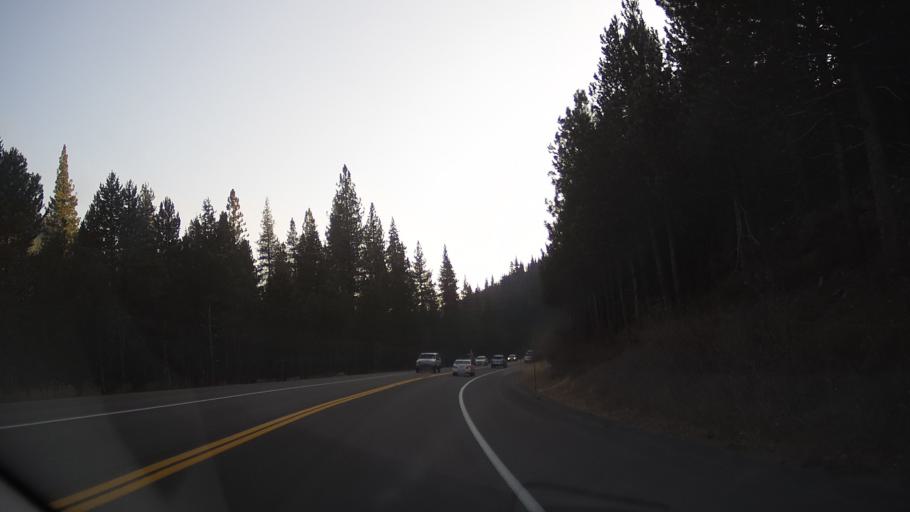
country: US
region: California
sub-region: Placer County
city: Sunnyside-Tahoe City
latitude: 39.2211
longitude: -120.2020
